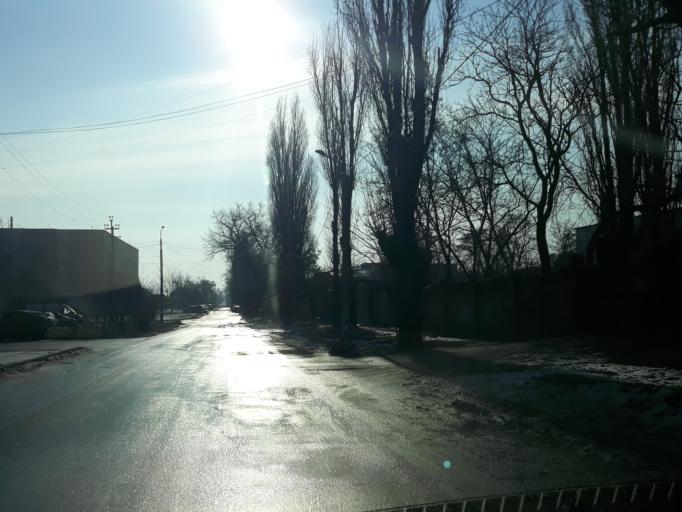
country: RU
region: Rostov
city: Taganrog
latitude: 47.2268
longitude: 38.9073
